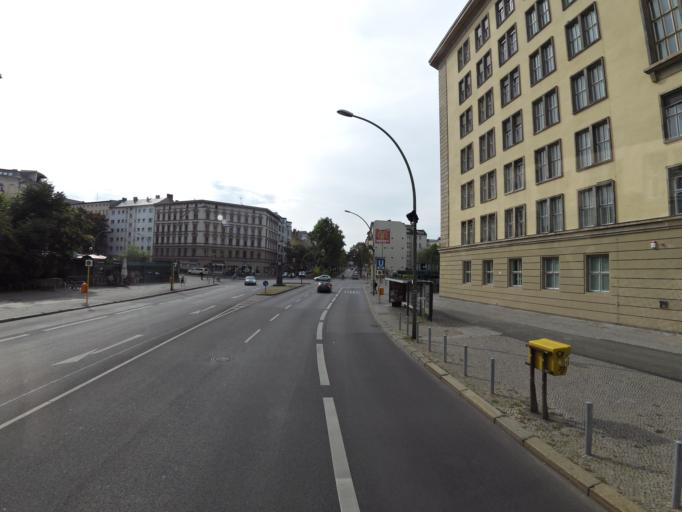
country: DE
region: Berlin
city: Berlin Schoeneberg
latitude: 52.4911
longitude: 13.3607
